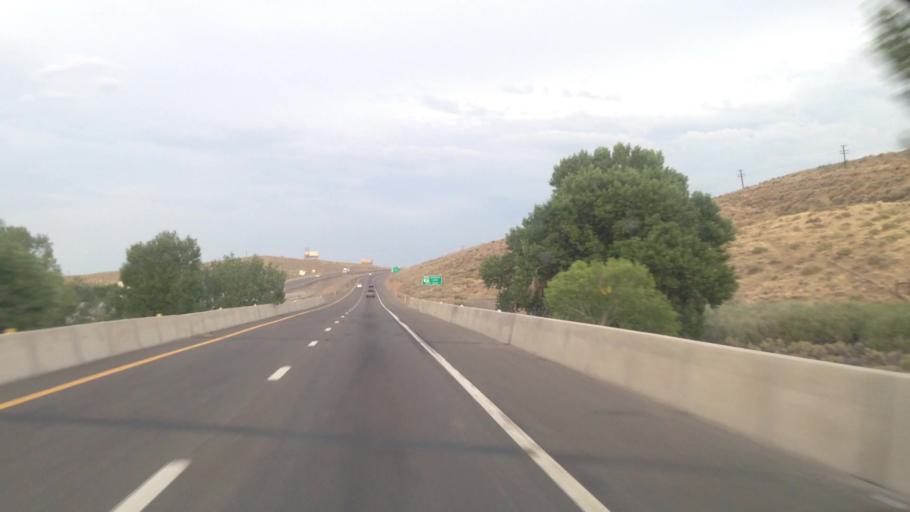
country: US
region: Nevada
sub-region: Lyon County
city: Fernley
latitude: 39.6177
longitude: -119.2943
